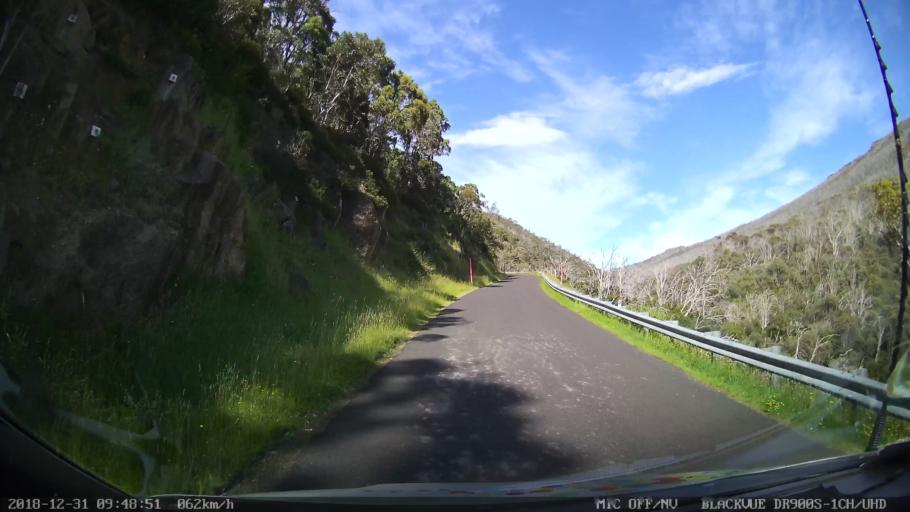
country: AU
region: New South Wales
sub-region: Snowy River
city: Jindabyne
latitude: -36.5145
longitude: 148.2884
